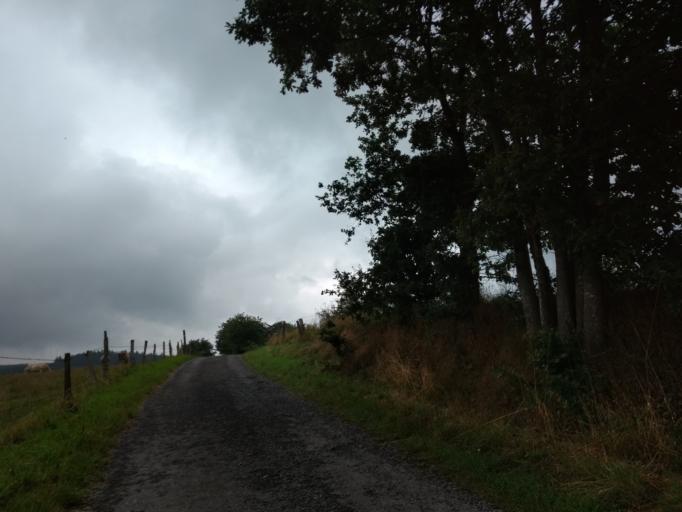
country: BE
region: Wallonia
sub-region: Province du Luxembourg
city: Houffalize
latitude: 50.1450
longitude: 5.7625
